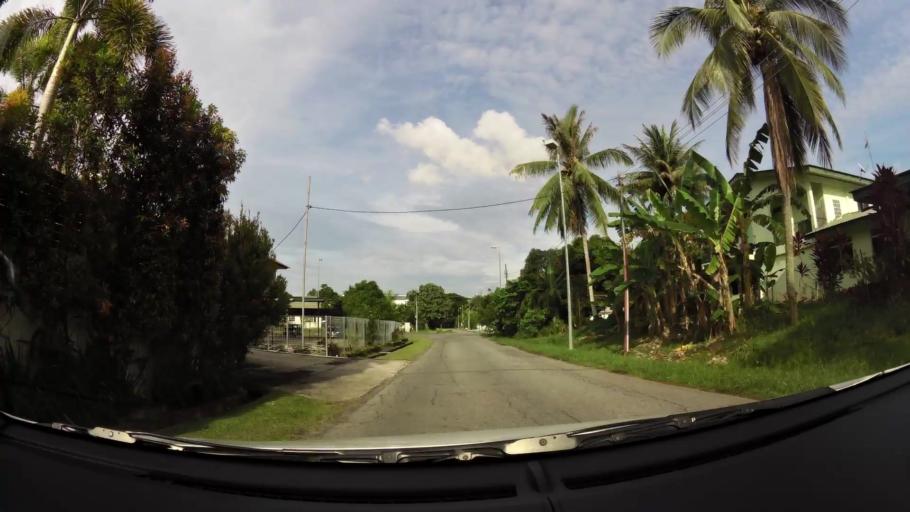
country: BN
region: Brunei and Muara
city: Bandar Seri Begawan
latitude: 4.9098
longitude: 114.8939
